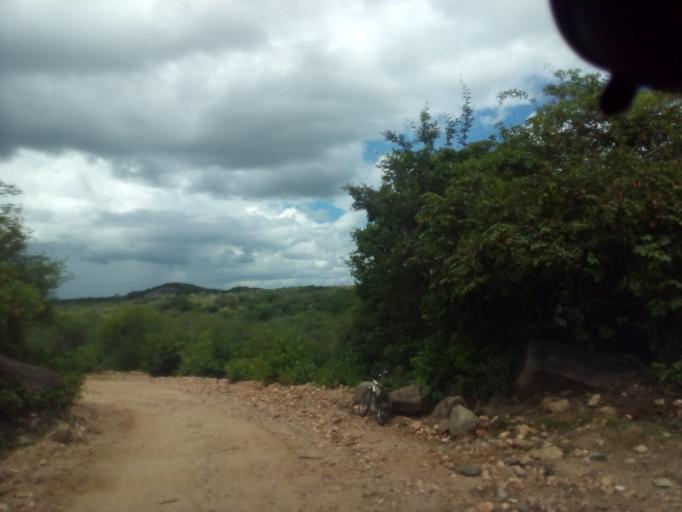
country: BR
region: Rio Grande do Norte
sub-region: Sao Tome
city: Sao Tome
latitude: -5.9519
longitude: -35.9218
